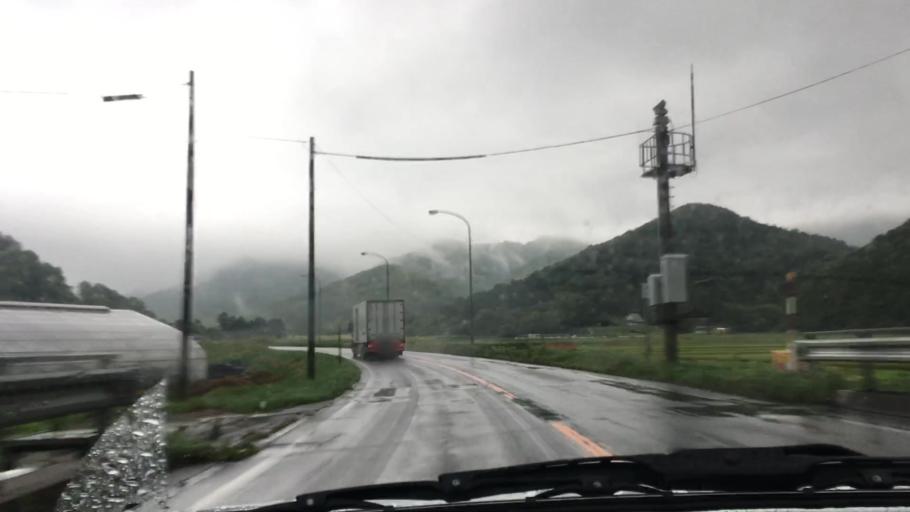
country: JP
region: Hokkaido
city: Niseko Town
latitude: 42.6005
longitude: 140.5876
